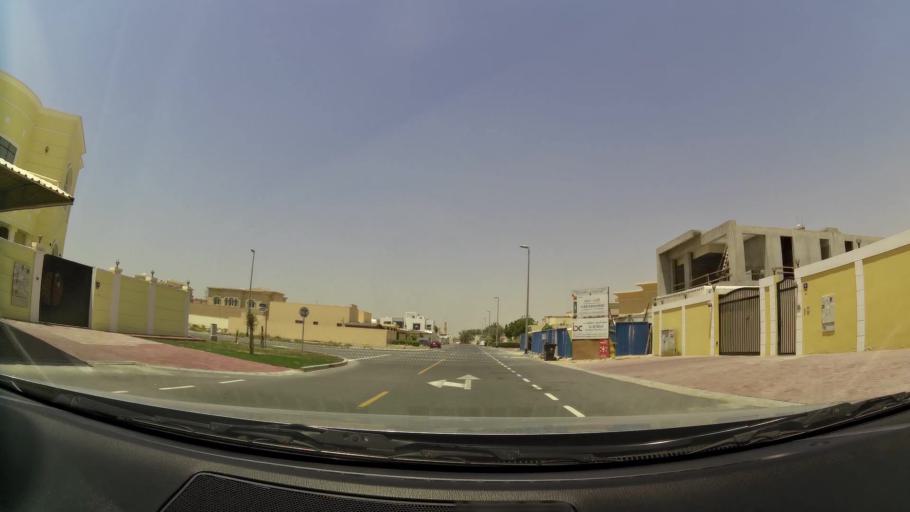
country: AE
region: Dubai
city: Dubai
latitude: 25.0849
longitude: 55.2108
